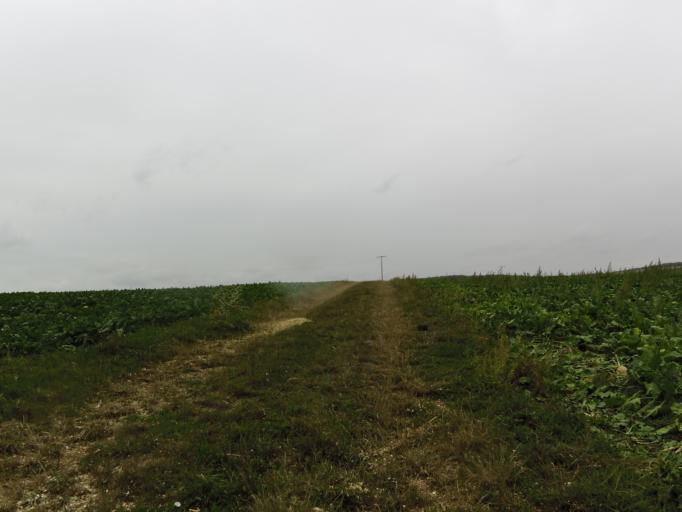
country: DE
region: Bavaria
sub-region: Regierungsbezirk Unterfranken
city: Rimpar
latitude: 49.8517
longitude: 9.9415
